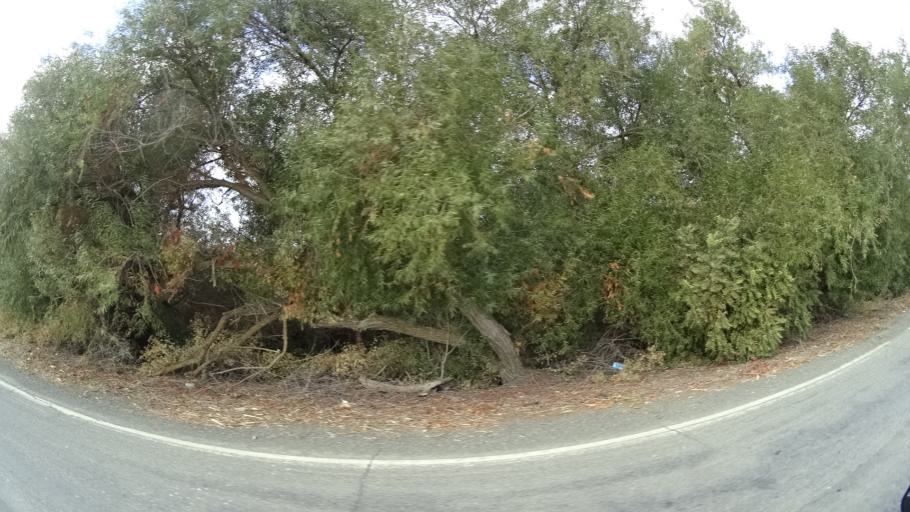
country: US
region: California
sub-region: Yolo County
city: Woodland
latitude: 38.8040
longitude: -121.7744
